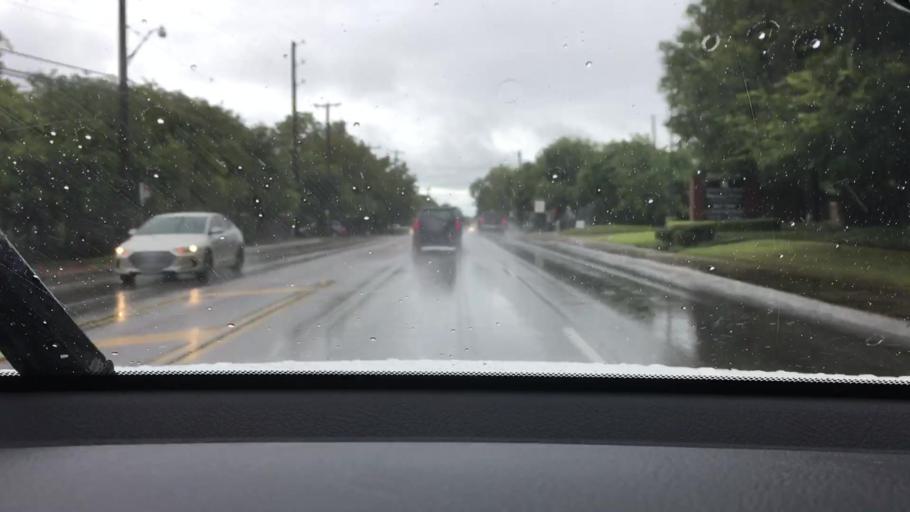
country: US
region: Texas
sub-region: Bexar County
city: Alamo Heights
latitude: 29.4959
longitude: -98.4666
